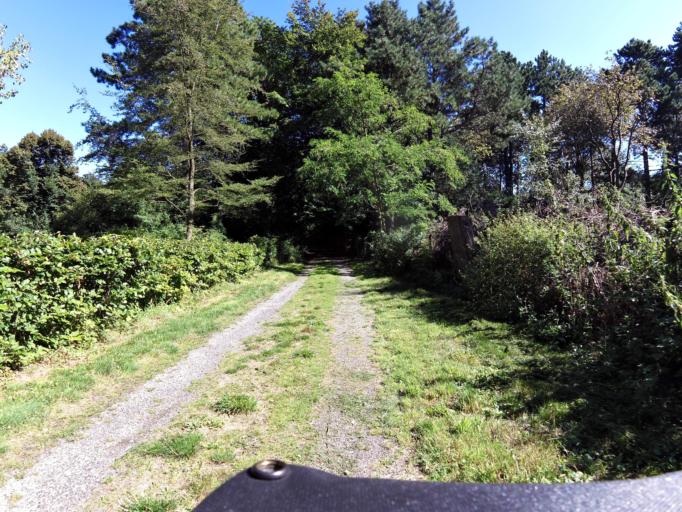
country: NL
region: South Holland
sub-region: Gemeente Hellevoetsluis
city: Nieuw-Helvoet
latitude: 51.8908
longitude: 4.0498
